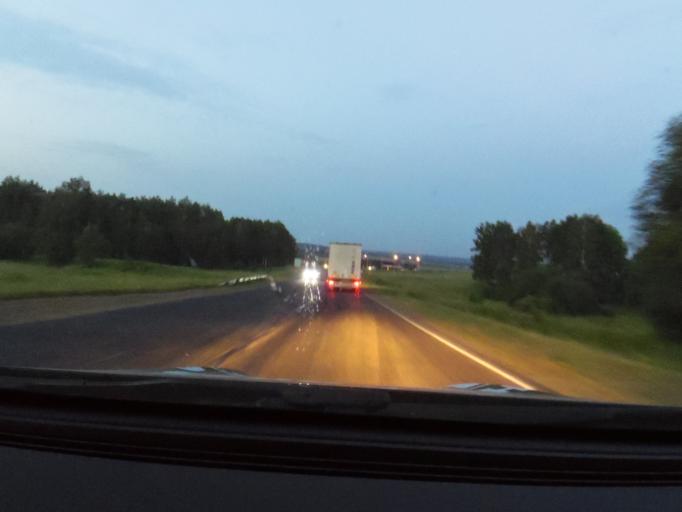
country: RU
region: Bashkortostan
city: Duvan
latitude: 56.0703
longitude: 58.1735
